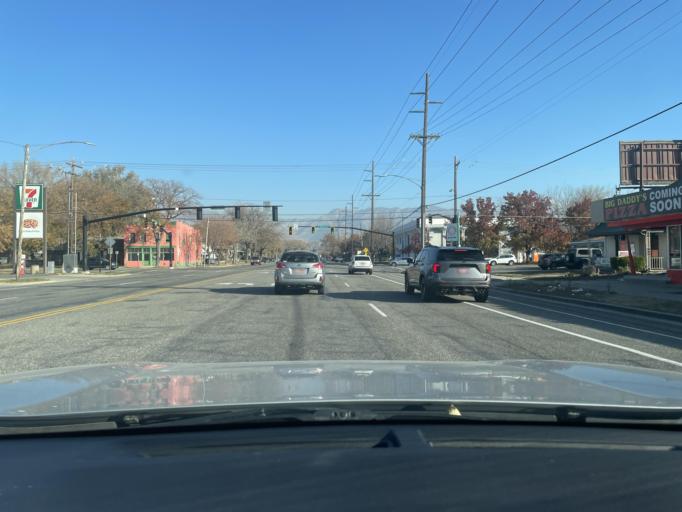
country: US
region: Utah
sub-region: Salt Lake County
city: Salt Lake City
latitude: 40.7519
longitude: -111.8863
